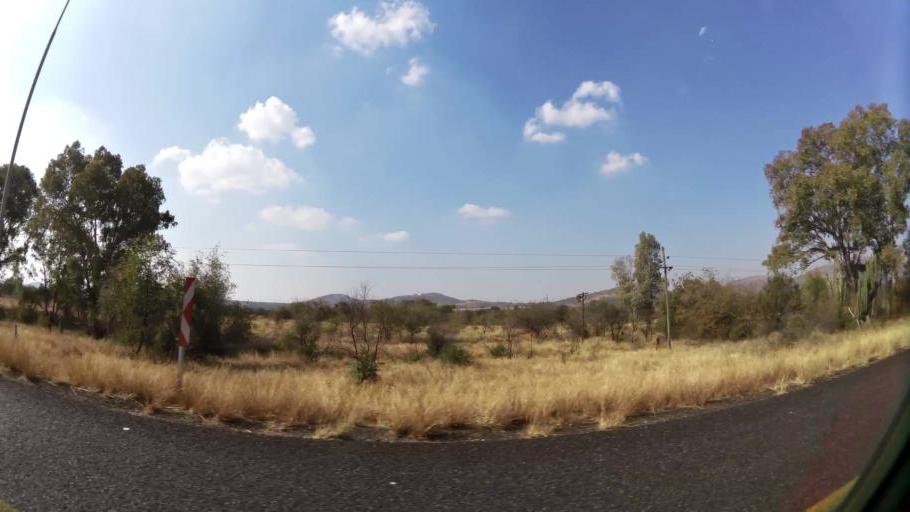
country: ZA
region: North-West
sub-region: Bojanala Platinum District Municipality
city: Rustenburg
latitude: -25.6240
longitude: 27.1571
